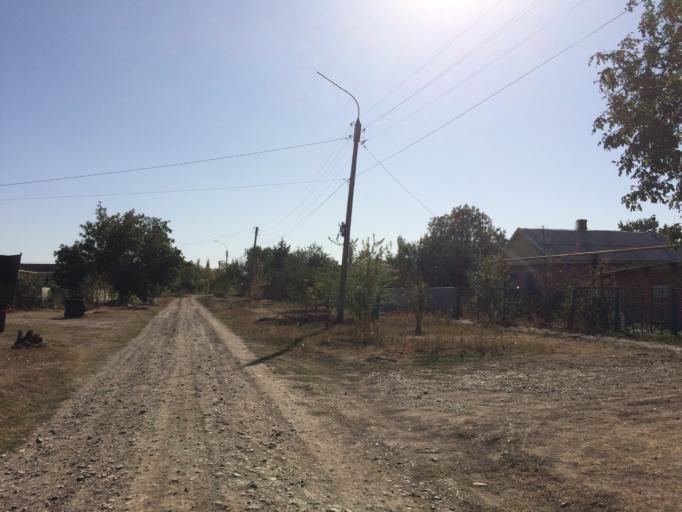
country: RU
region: Rostov
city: Tselina
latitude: 46.5209
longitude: 41.1837
